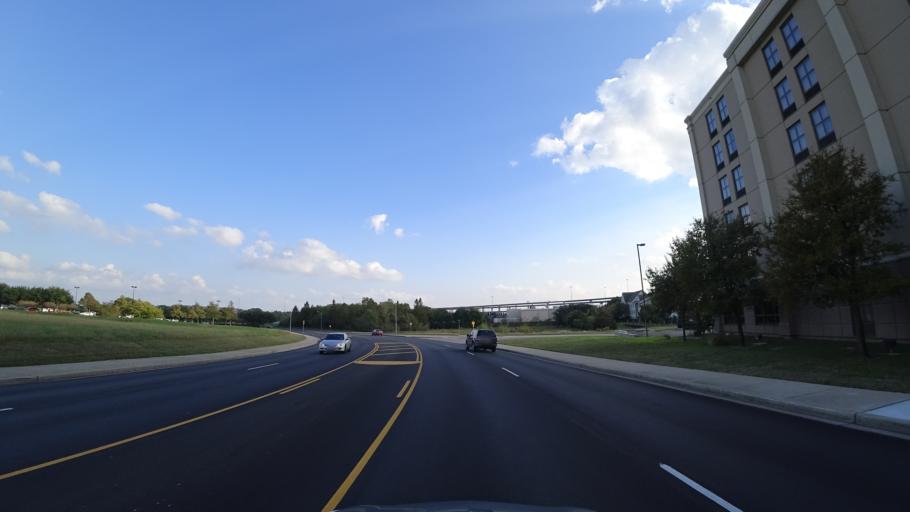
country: US
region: Texas
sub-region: Williamson County
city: Round Rock
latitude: 30.4874
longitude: -97.6736
